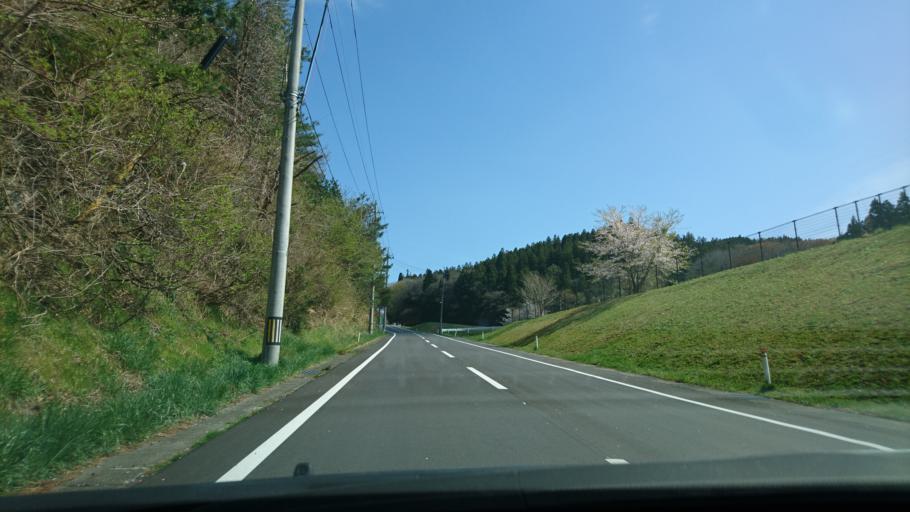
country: JP
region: Iwate
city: Ofunato
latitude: 38.9339
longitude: 141.4499
